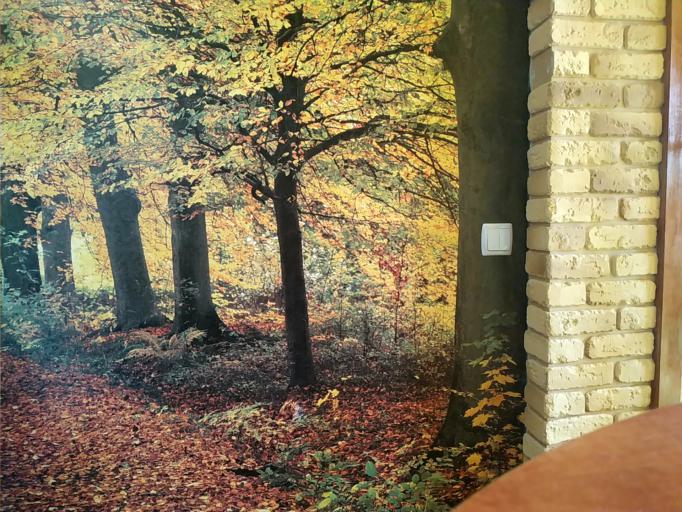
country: RU
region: Jaroslavl
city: Kukoboy
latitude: 58.8789
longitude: 39.7128
